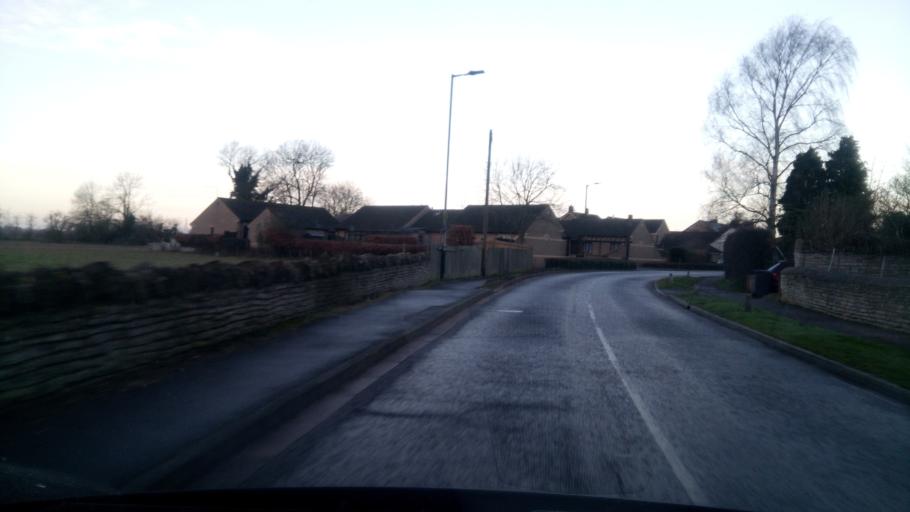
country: GB
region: England
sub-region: Peterborough
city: Castor
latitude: 52.5737
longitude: -0.3493
